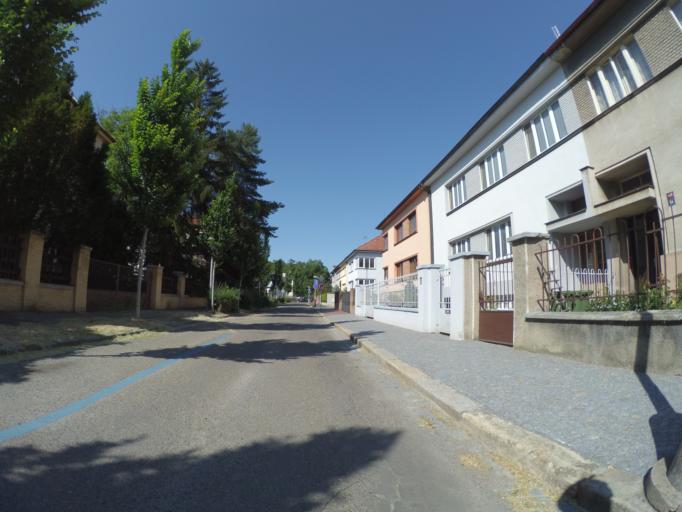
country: CZ
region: Central Bohemia
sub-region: Okres Nymburk
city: Podebrady
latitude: 50.1496
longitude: 15.1197
